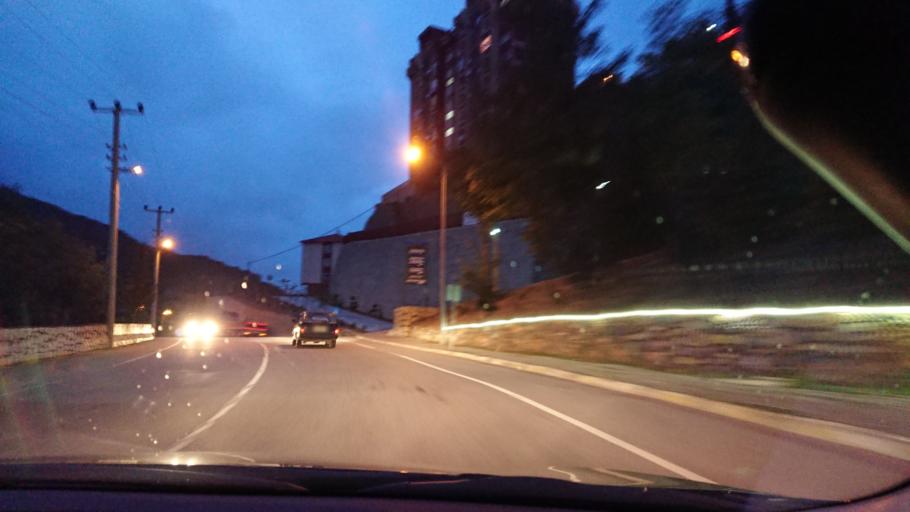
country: TR
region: Gumushane
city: Kurtun
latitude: 40.6716
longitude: 39.1400
